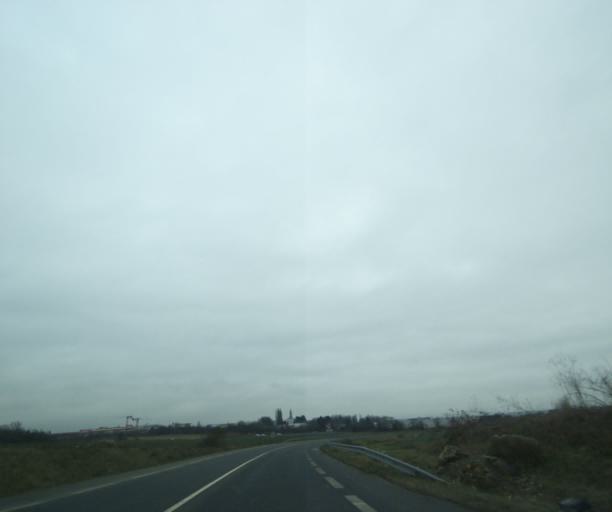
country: FR
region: Ile-de-France
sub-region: Departement de l'Essonne
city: Champlan
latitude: 48.7087
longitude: 2.2833
